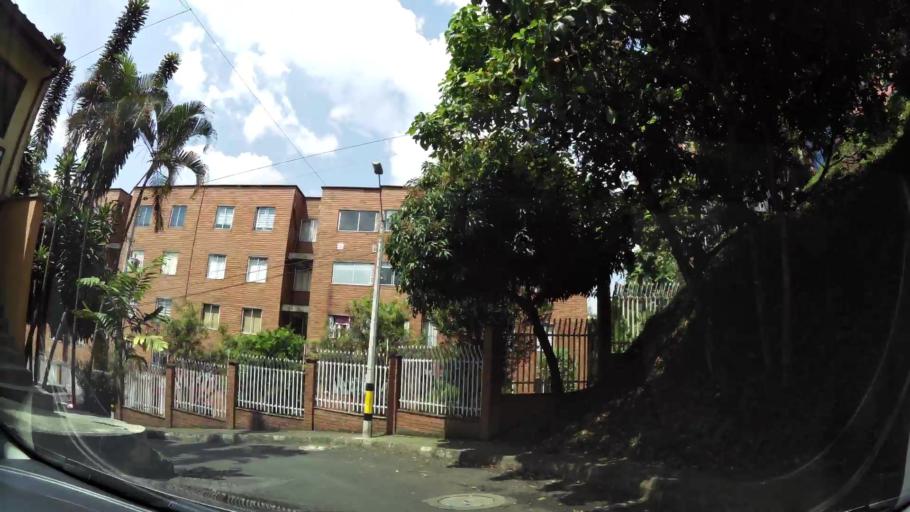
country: CO
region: Antioquia
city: Envigado
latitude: 6.1704
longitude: -75.5912
